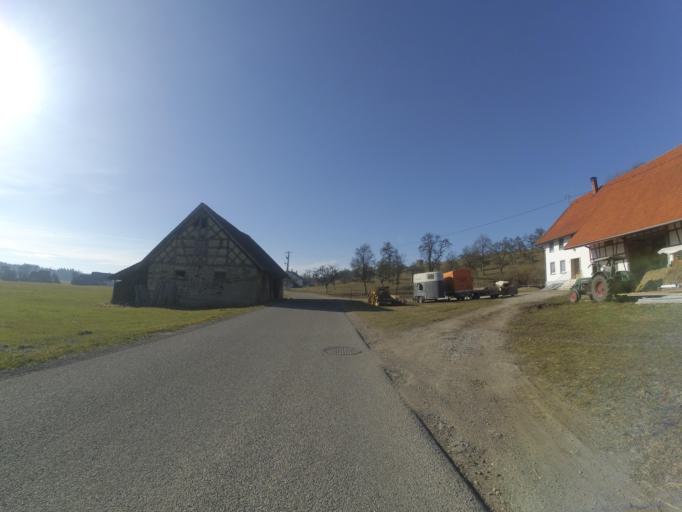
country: DE
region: Baden-Wuerttemberg
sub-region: Tuebingen Region
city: Wolpertswende
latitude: 47.9068
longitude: 9.6216
